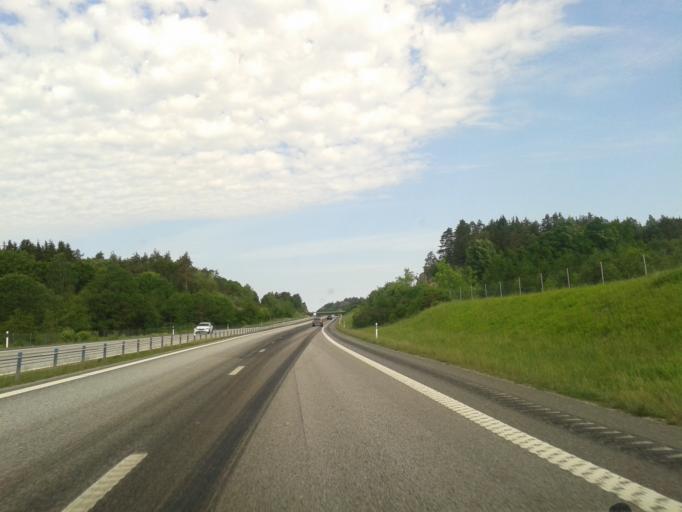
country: SE
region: Vaestra Goetaland
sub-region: Lysekils Kommun
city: Brastad
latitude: 58.5441
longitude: 11.5190
